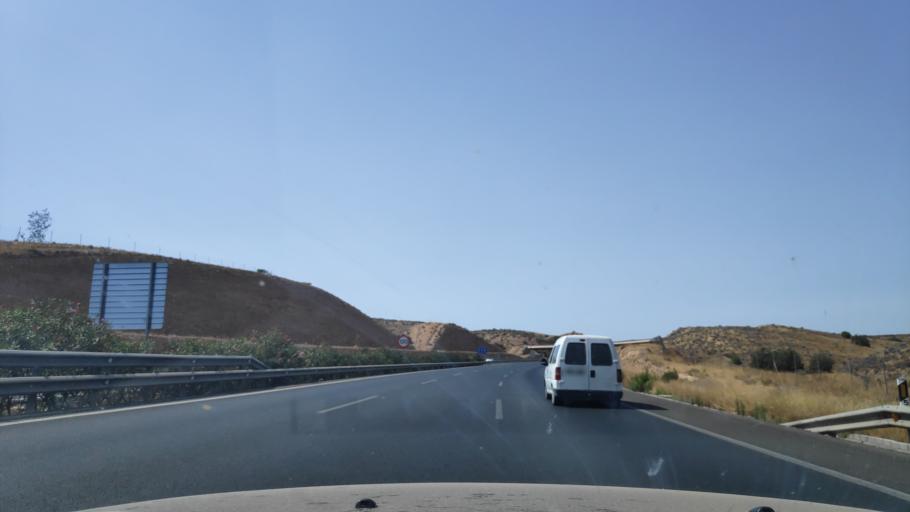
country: ES
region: Murcia
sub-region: Murcia
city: Molina de Segura
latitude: 38.0341
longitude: -1.1592
